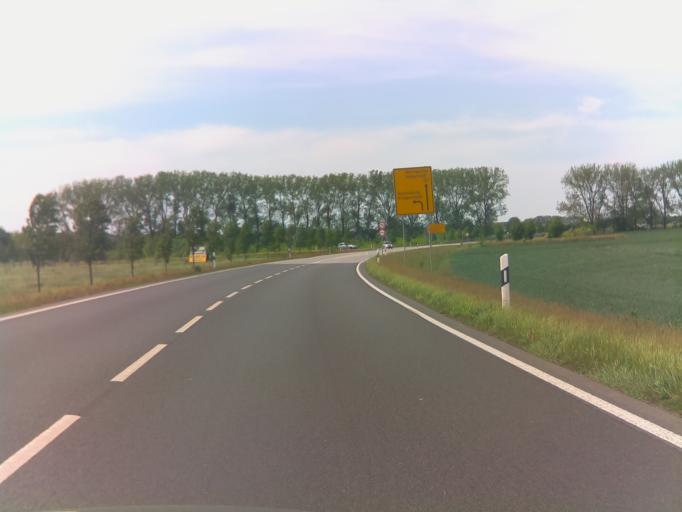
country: DE
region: Saxony-Anhalt
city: Kroppenstedt
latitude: 51.9402
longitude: 11.3324
